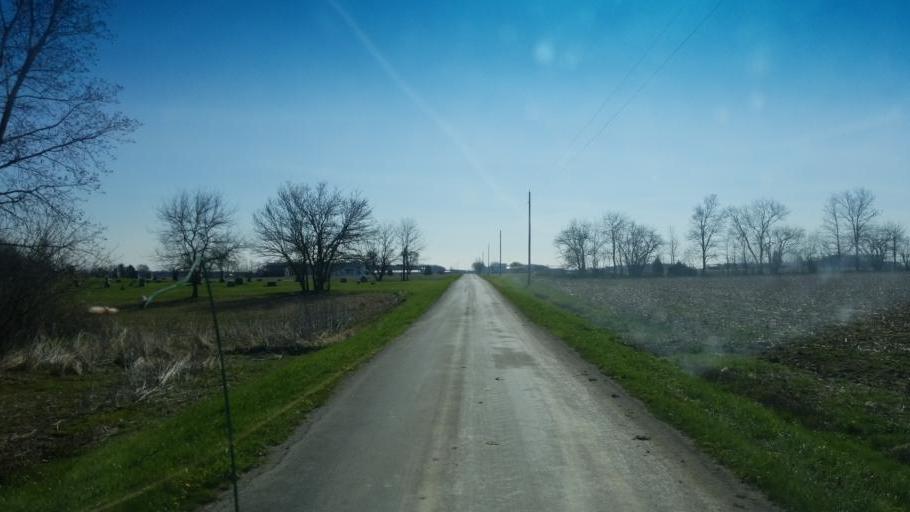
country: US
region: Ohio
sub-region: Hardin County
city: Forest
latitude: 40.7087
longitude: -83.4841
